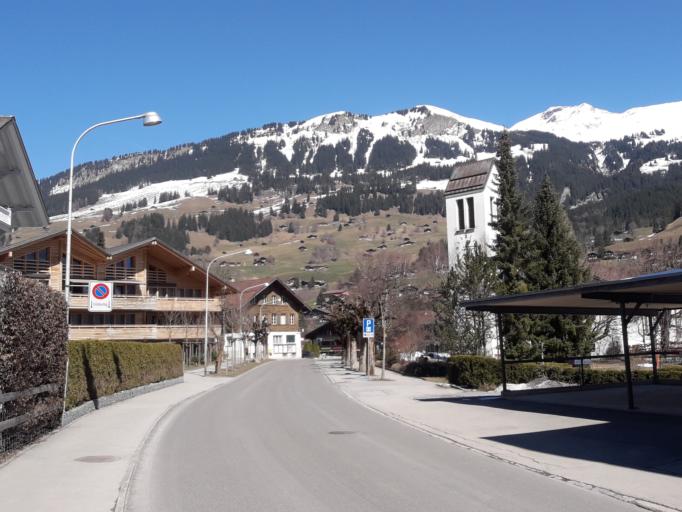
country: CH
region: Bern
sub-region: Obersimmental-Saanen District
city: Lenk
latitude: 46.4558
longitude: 7.4400
